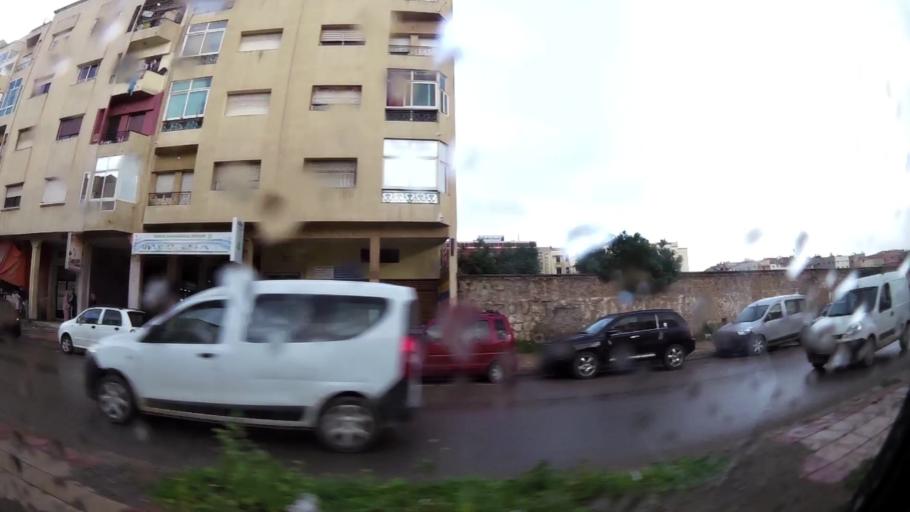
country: MA
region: Grand Casablanca
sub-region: Mohammedia
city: Mohammedia
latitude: 33.6778
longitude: -7.3876
